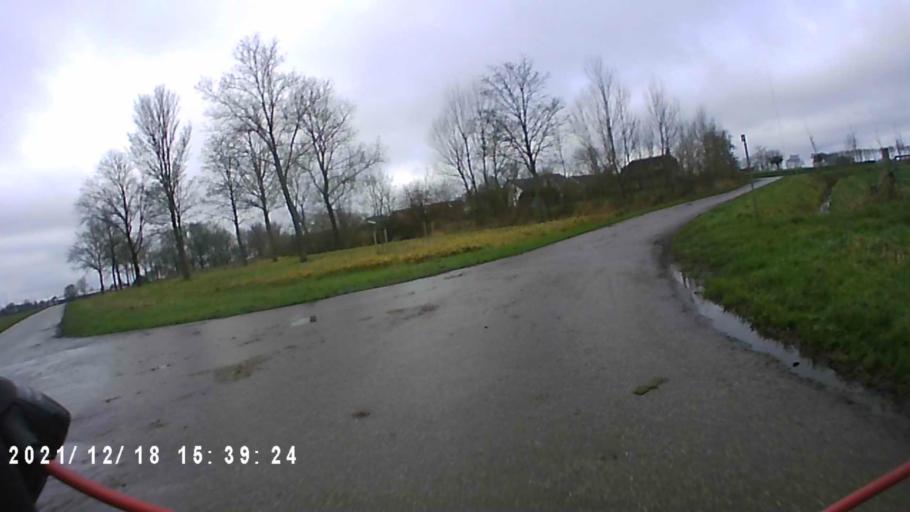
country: NL
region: Friesland
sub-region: Gemeente Dongeradeel
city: Anjum
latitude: 53.3374
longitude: 6.1150
